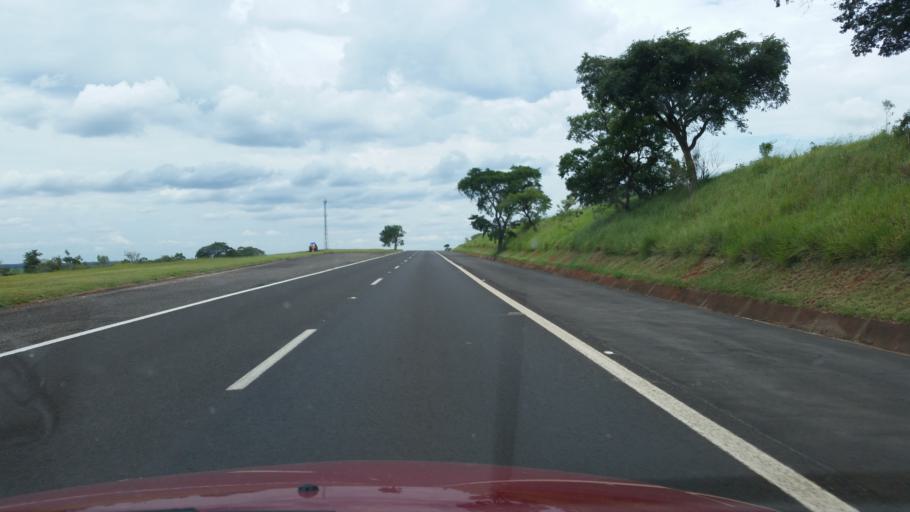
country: BR
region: Sao Paulo
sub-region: Avare
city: Avare
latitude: -22.9665
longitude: -48.8092
